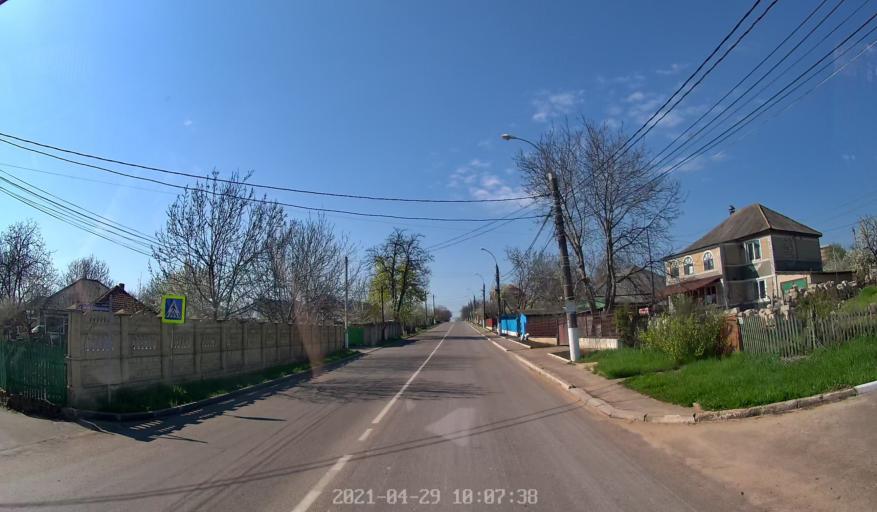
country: MD
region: Chisinau
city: Cricova
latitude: 47.1338
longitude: 28.8664
